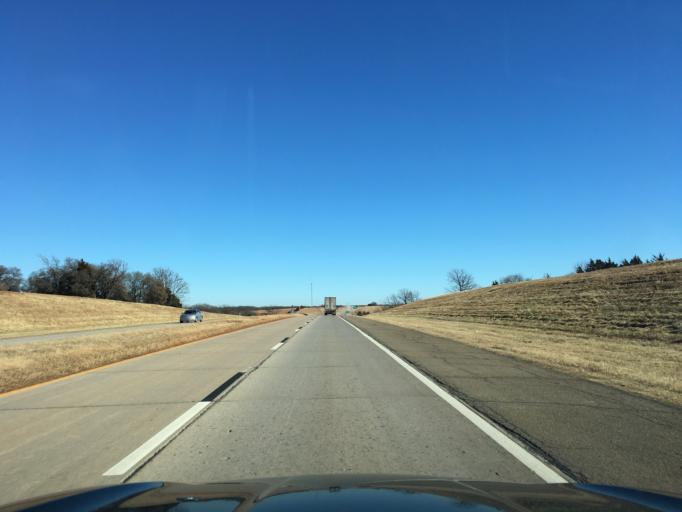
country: US
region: Oklahoma
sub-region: Pawnee County
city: Pawnee
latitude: 36.2248
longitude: -96.7724
